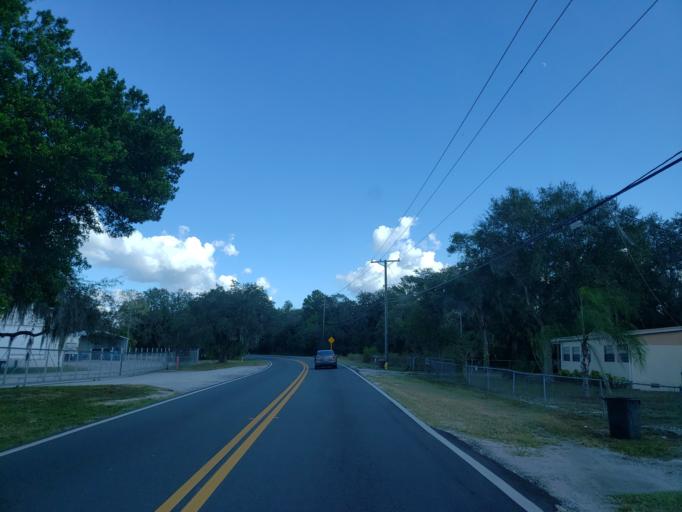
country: US
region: Florida
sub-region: Hillsborough County
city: Dover
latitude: 28.0038
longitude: -82.1682
